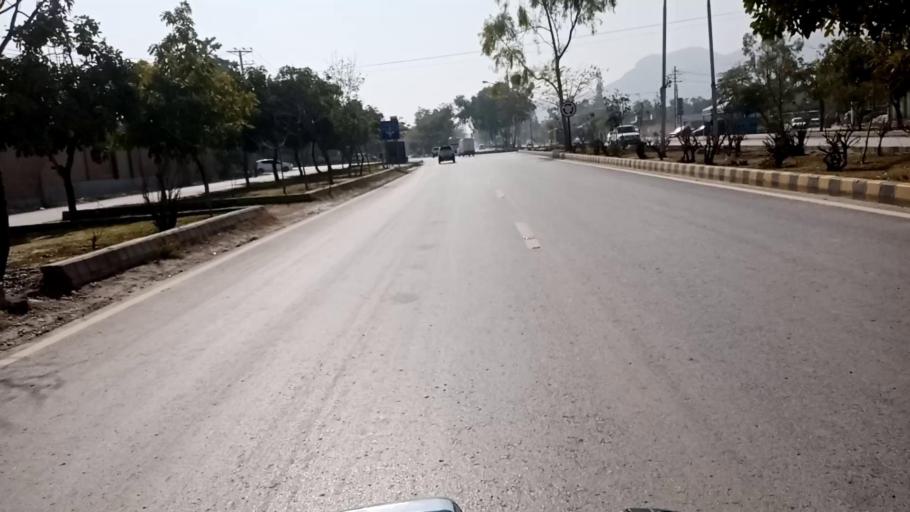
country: PK
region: Khyber Pakhtunkhwa
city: Peshawar
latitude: 33.9574
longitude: 71.4330
